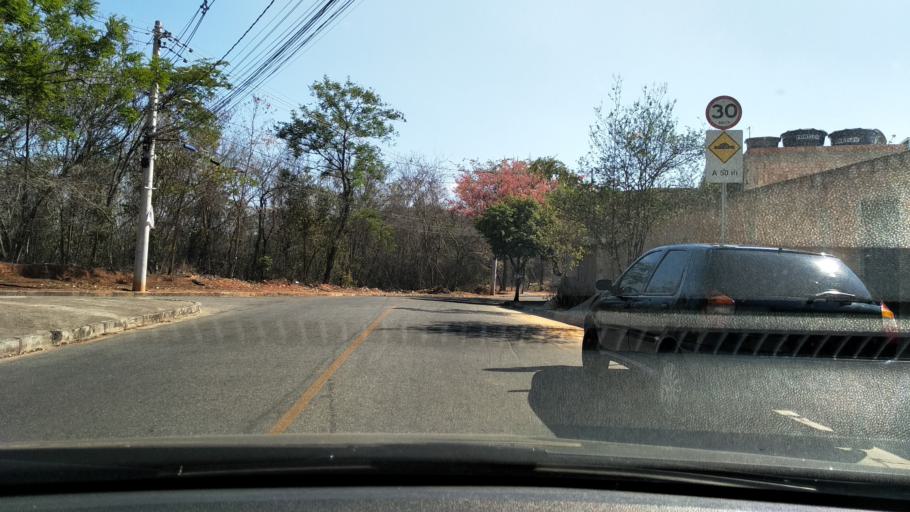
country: BR
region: Minas Gerais
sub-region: Belo Horizonte
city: Belo Horizonte
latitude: -19.8613
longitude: -43.8774
